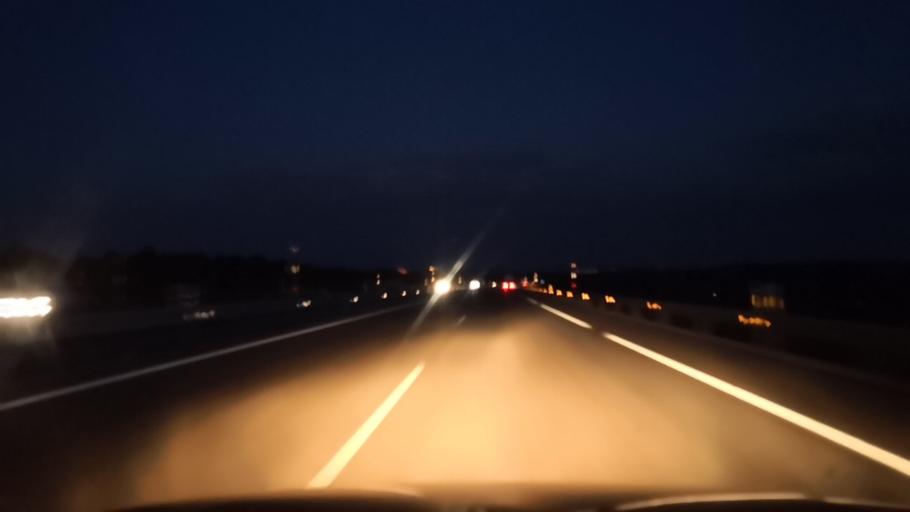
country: ES
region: Castille and Leon
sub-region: Provincia de Leon
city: Brazuelo
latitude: 42.5606
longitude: -6.1964
